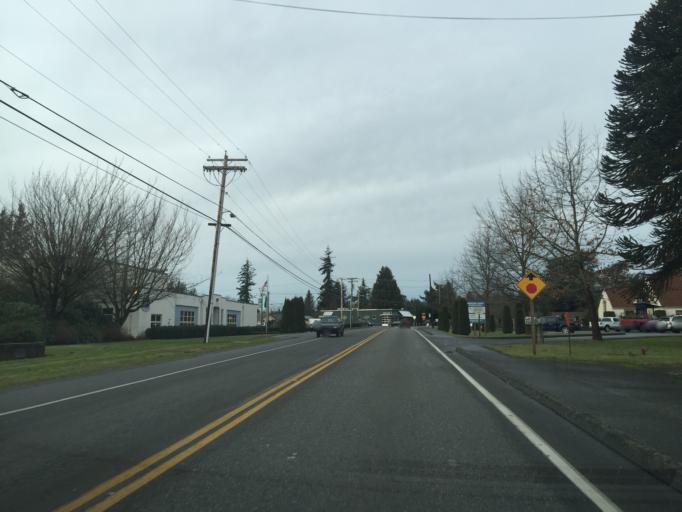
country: US
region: Washington
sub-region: Whatcom County
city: Marietta-Alderwood
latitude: 48.8321
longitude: -122.5399
